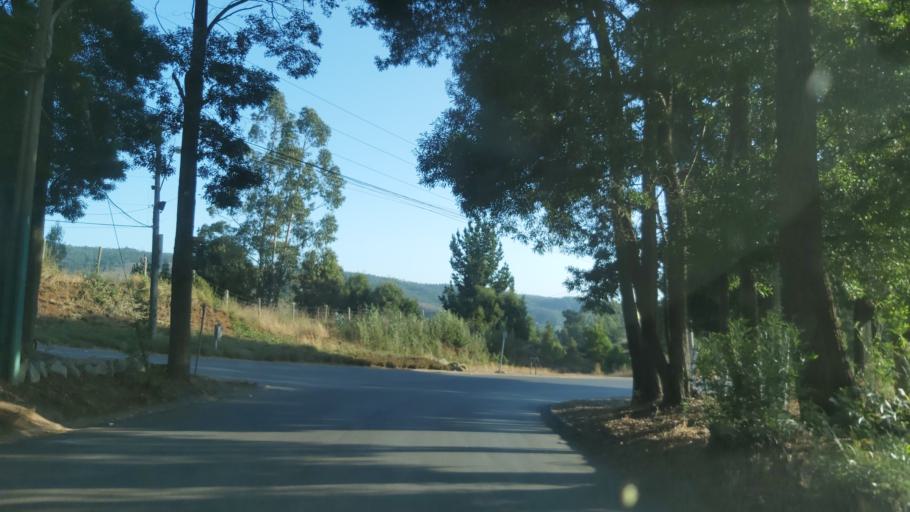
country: CL
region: Biobio
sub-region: Provincia de Concepcion
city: Tome
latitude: -36.5374
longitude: -72.9262
